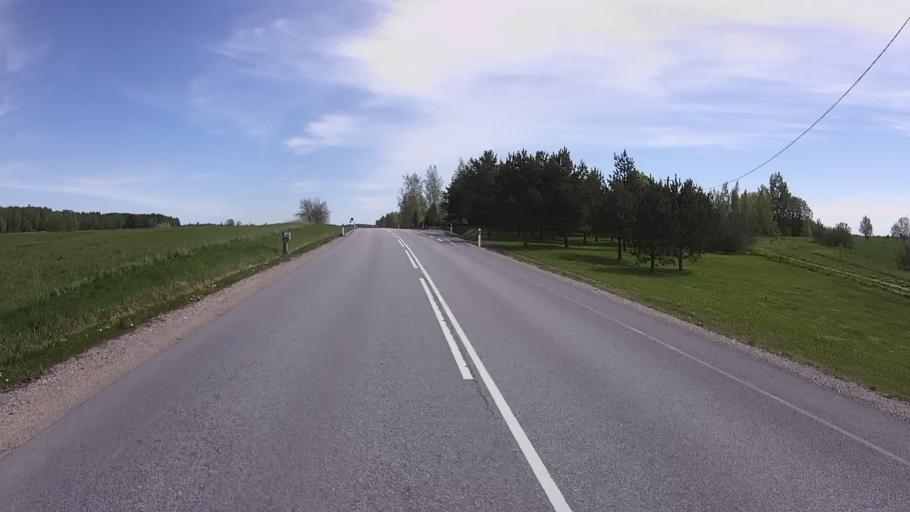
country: EE
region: Valgamaa
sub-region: Valga linn
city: Valga
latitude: 57.7263
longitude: 26.1820
